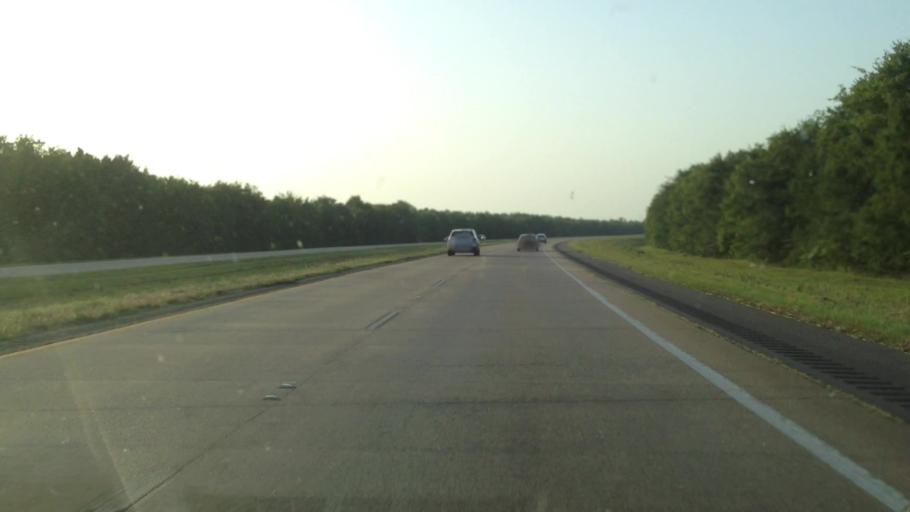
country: US
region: Louisiana
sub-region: Natchitoches Parish
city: Vienna Bend
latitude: 31.5665
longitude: -92.9915
